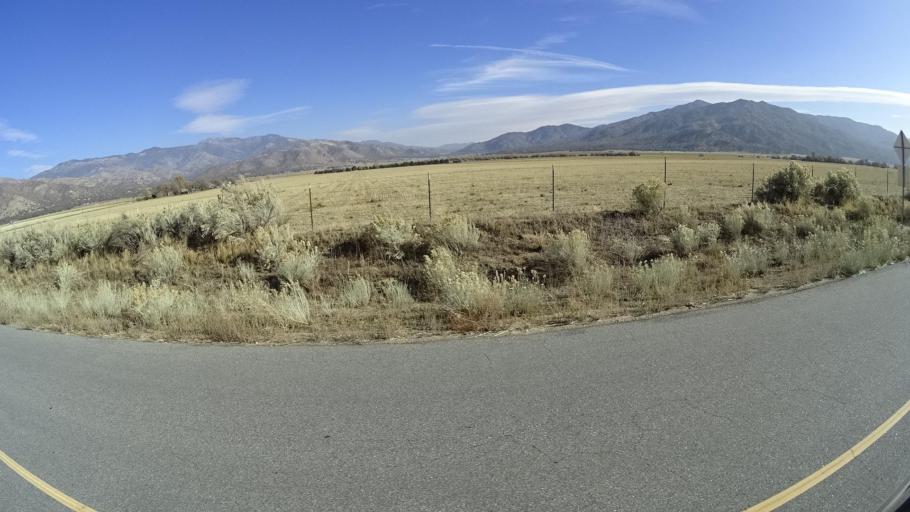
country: US
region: California
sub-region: Kern County
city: Bodfish
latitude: 35.4137
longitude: -118.5451
